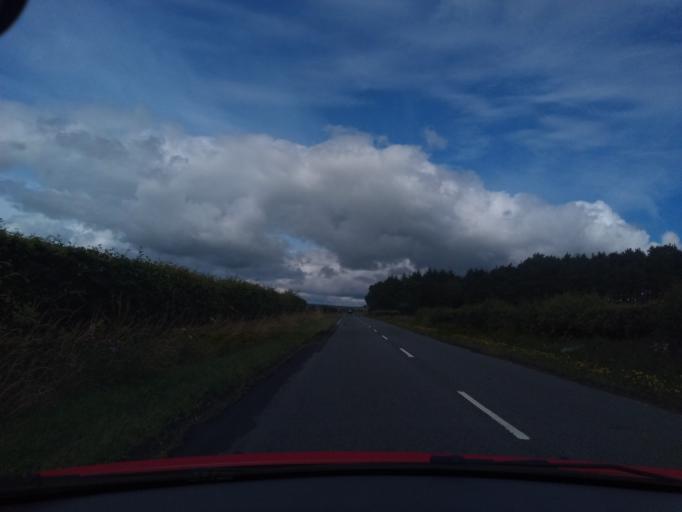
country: GB
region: Scotland
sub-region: The Scottish Borders
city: Lauder
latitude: 55.7331
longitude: -2.7355
